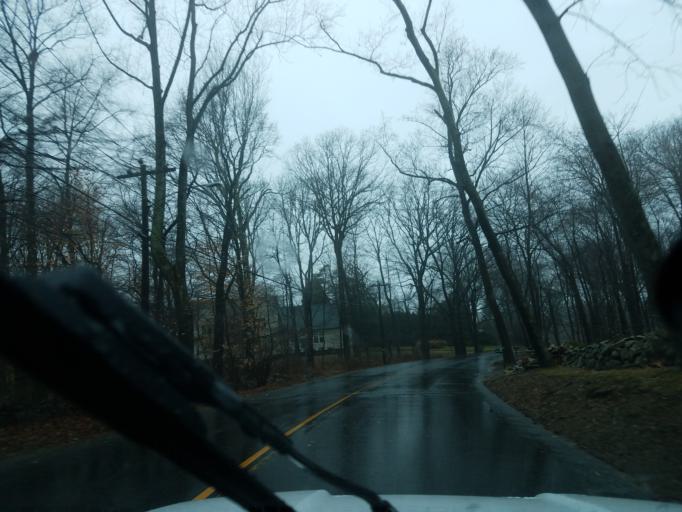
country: US
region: Connecticut
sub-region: Fairfield County
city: Darien
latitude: 41.0943
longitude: -73.5059
